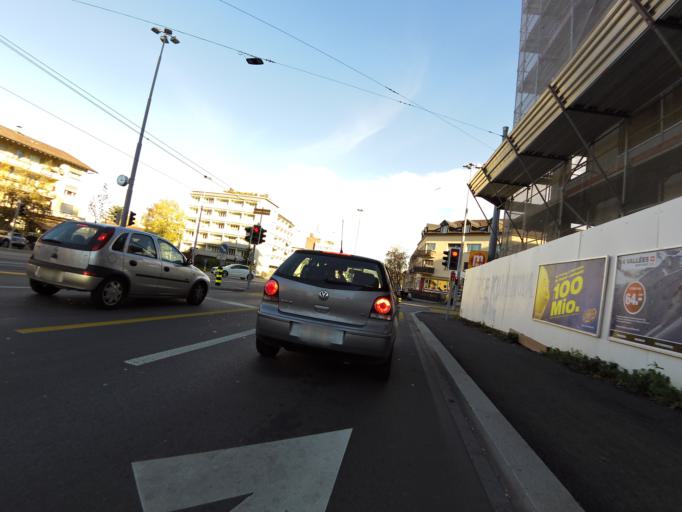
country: CH
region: Zurich
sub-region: Bezirk Zuerich
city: Zuerich (Kreis 3) / Friesenberg
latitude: 47.3687
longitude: 8.5008
